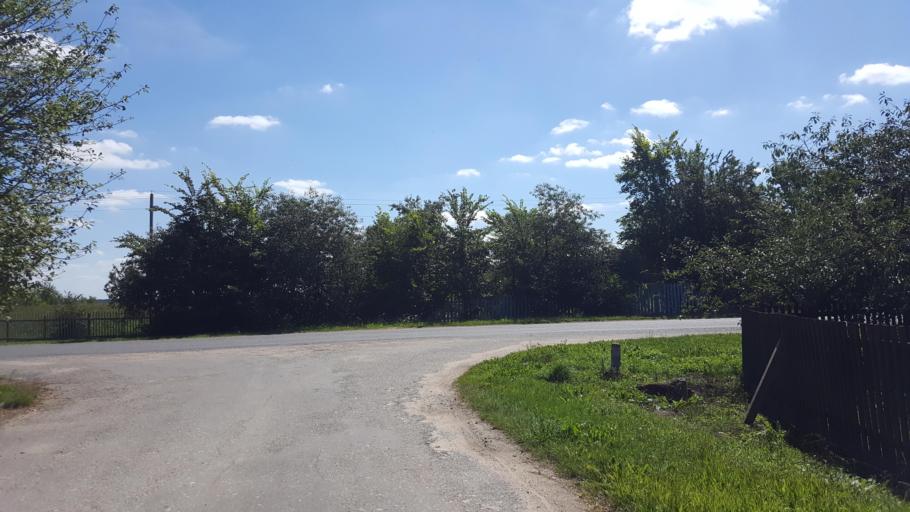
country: BY
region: Brest
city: Charnawchytsy
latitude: 52.3667
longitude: 23.6255
